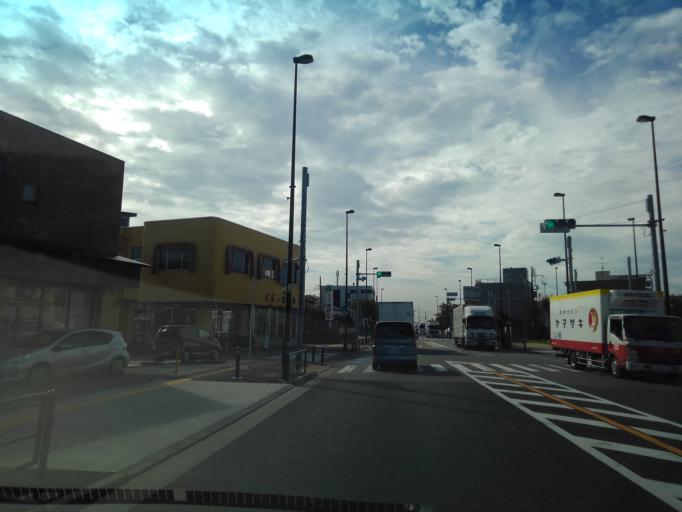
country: JP
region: Tokyo
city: Fussa
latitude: 35.7714
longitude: 139.3479
